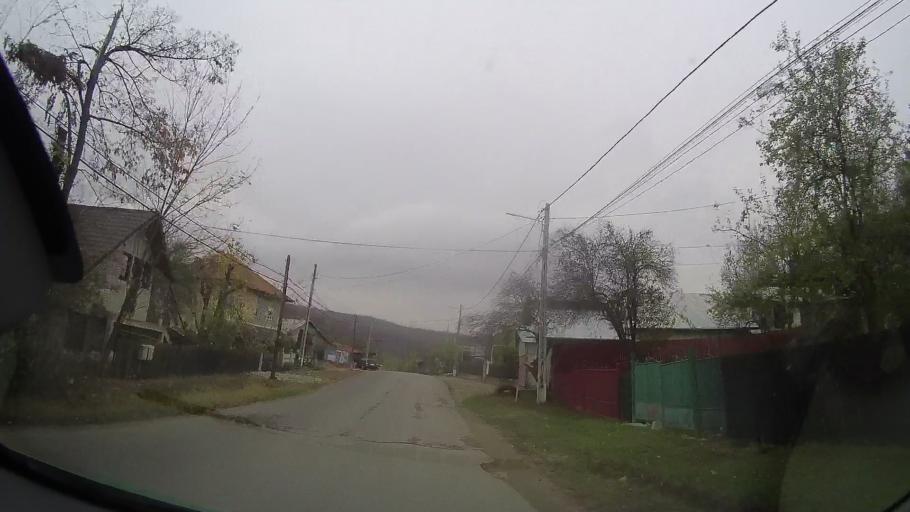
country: RO
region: Prahova
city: Ceptura de Sus
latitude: 45.0363
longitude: 26.3136
